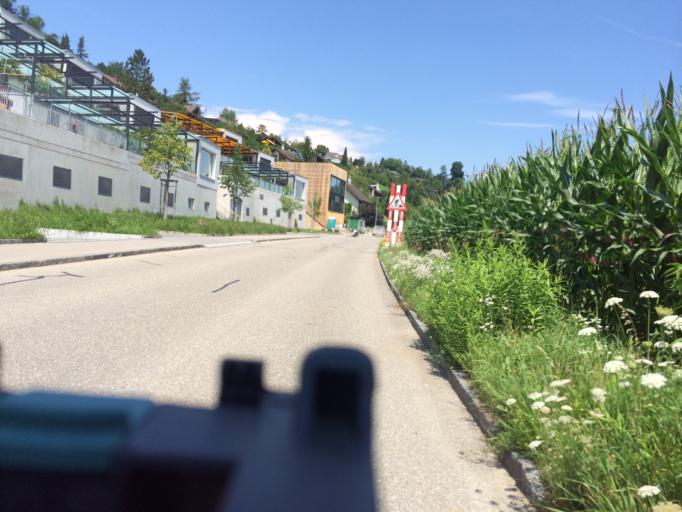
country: CH
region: Bern
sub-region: Bern-Mittelland District
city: Zollikofen
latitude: 46.9854
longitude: 7.4410
